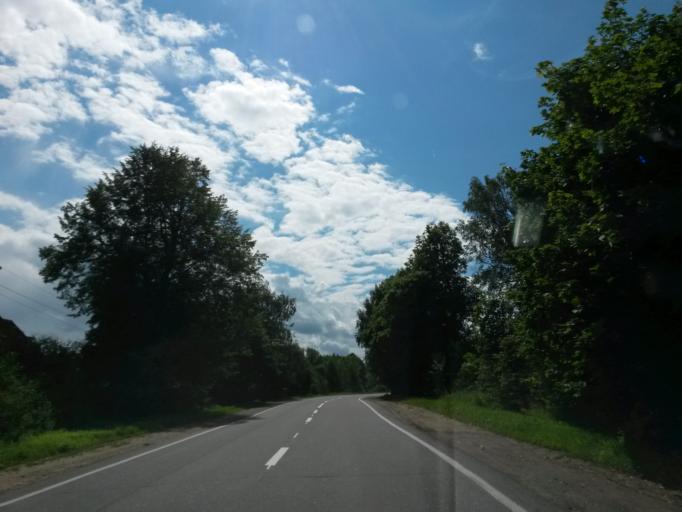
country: RU
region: Jaroslavl
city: Gavrilov-Yam
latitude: 57.2809
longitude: 39.9532
